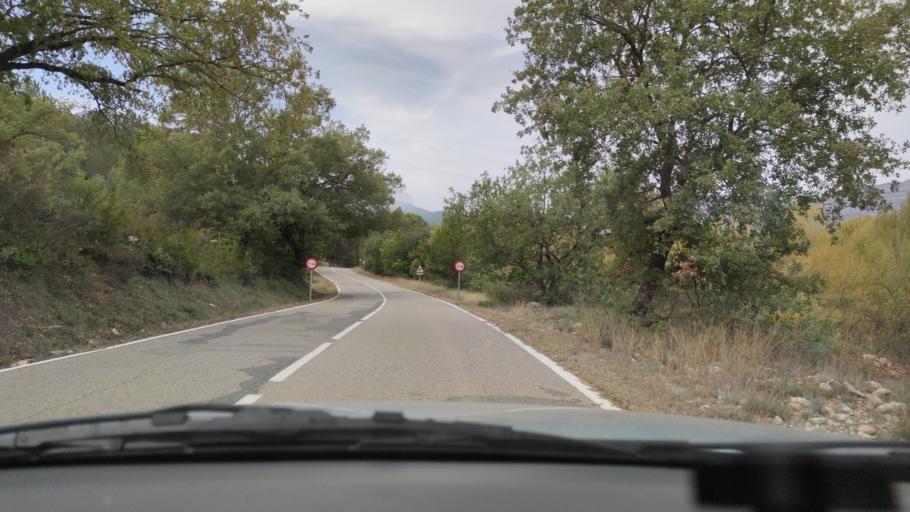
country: ES
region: Catalonia
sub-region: Provincia de Lleida
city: Llimiana
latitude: 42.0603
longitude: 0.8978
